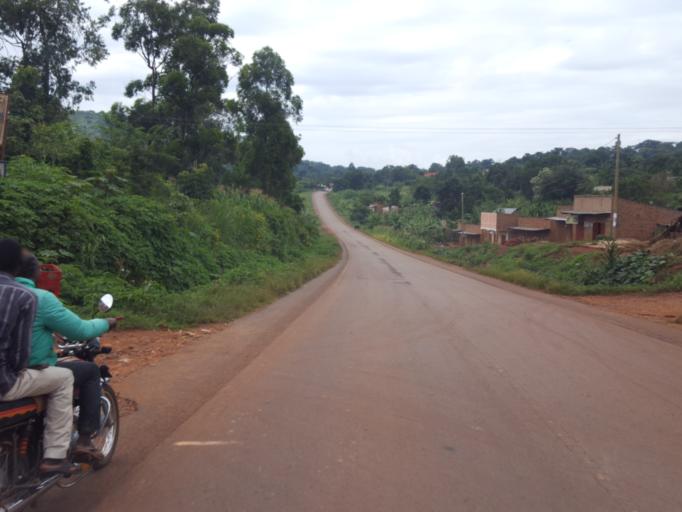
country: UG
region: Central Region
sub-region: Mityana District
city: Mityana
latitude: 0.6574
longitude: 32.0926
